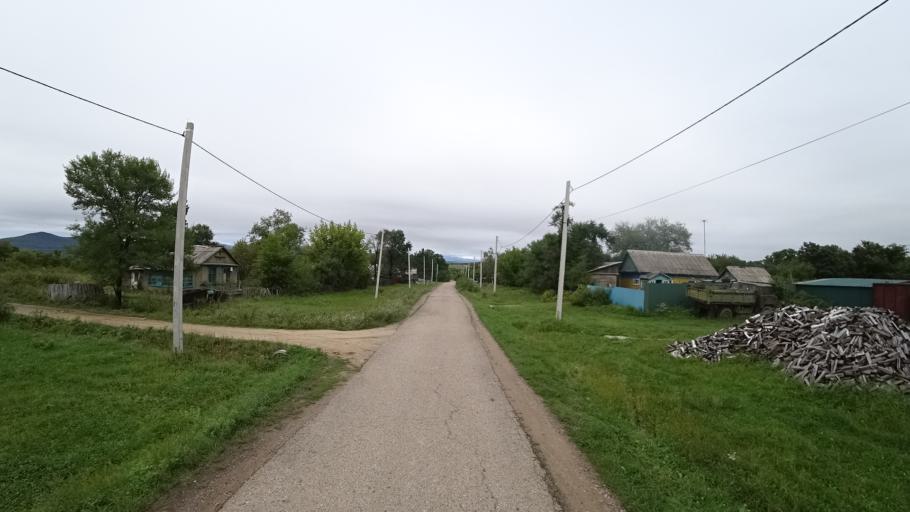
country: RU
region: Primorskiy
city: Monastyrishche
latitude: 44.0803
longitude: 132.5866
